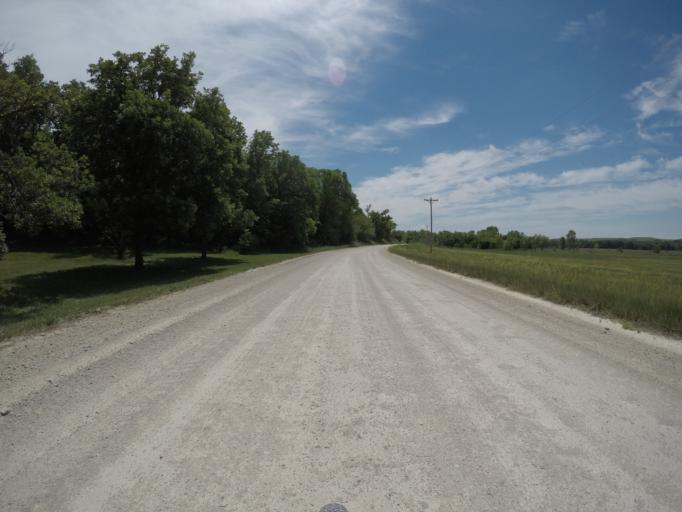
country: US
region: Kansas
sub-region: Wabaunsee County
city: Alma
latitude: 38.9838
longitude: -96.2668
